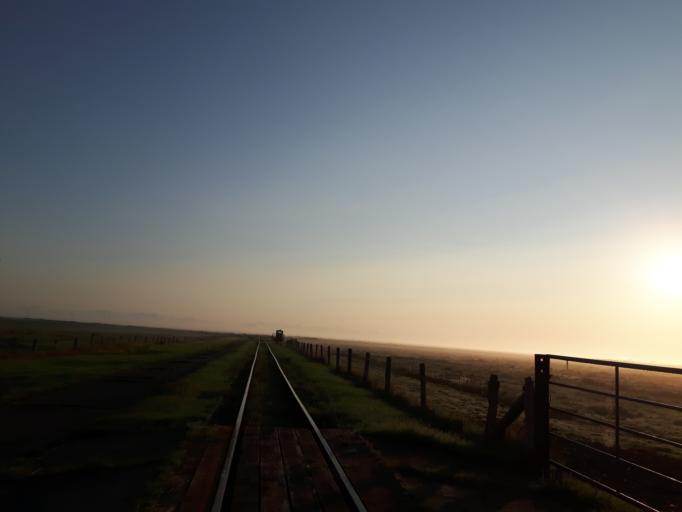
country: DE
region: Schleswig-Holstein
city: Grode
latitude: 54.6783
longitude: 8.7064
